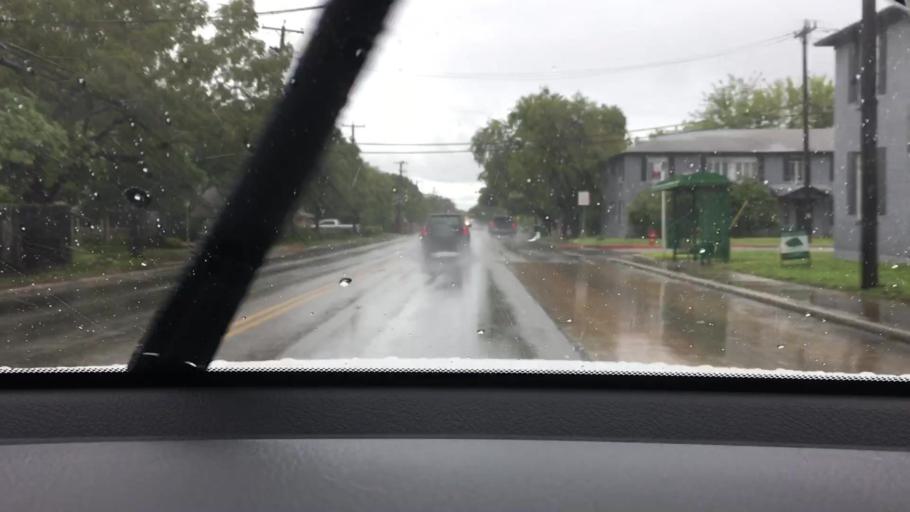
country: US
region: Texas
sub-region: Bexar County
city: Alamo Heights
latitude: 29.4952
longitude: -98.4666
